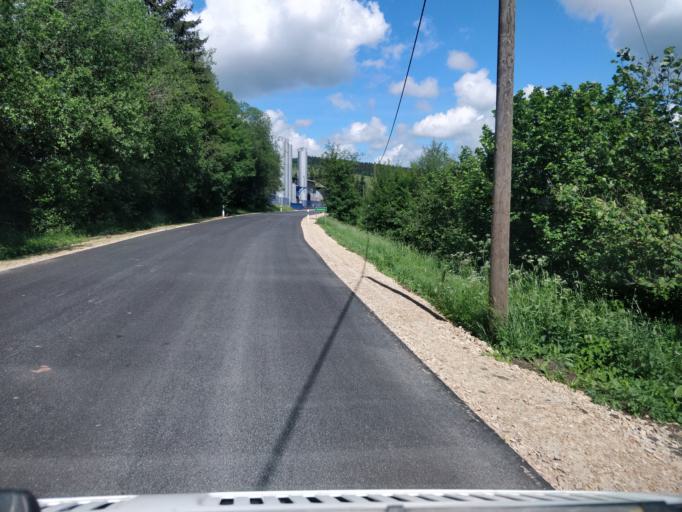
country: DE
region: Rheinland-Pfalz
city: Hallschlag
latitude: 50.3633
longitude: 6.4486
